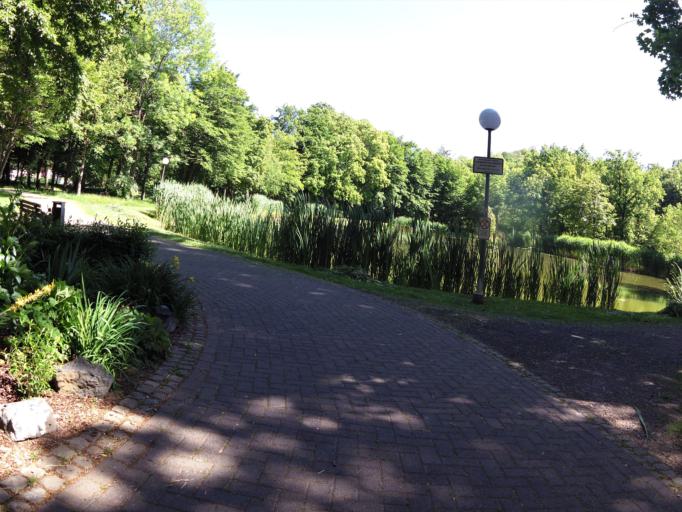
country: DE
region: Hesse
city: Philippsthal
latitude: 50.8397
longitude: 10.0034
